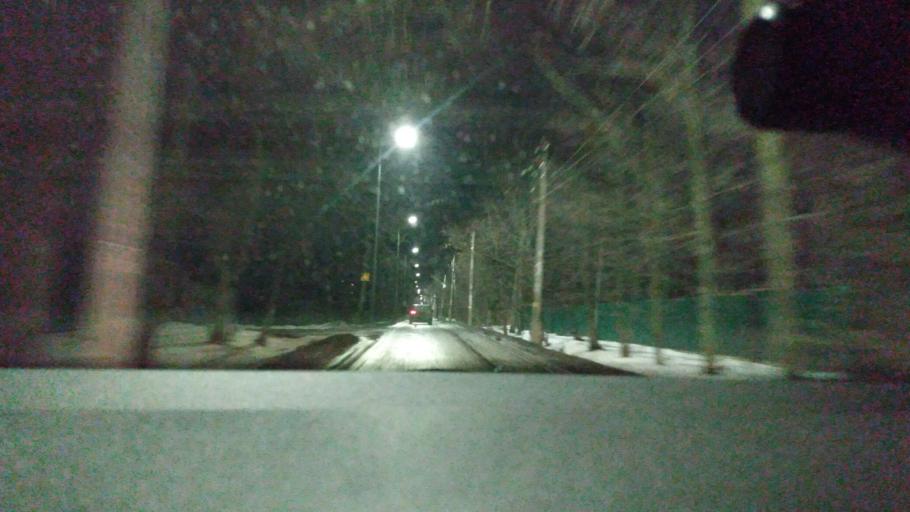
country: RU
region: Moskovskaya
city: Saltykovka
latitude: 55.7573
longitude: 37.9375
